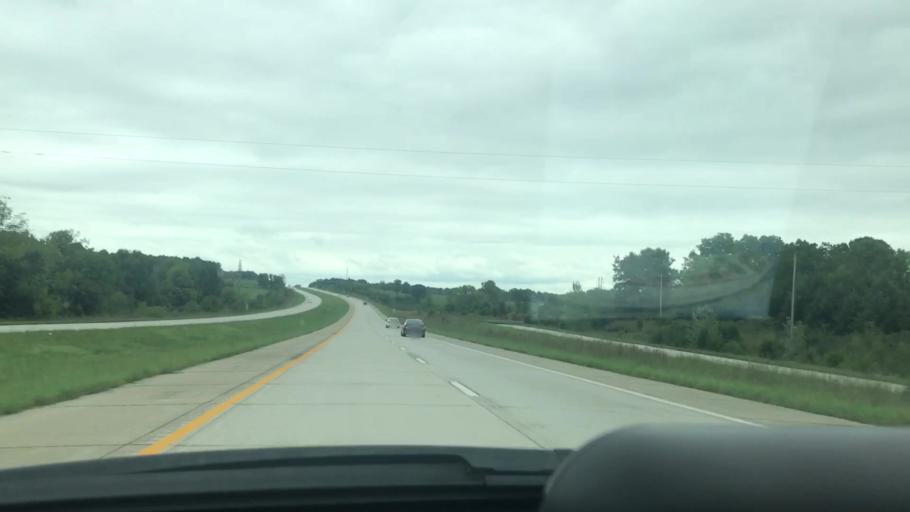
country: US
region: Missouri
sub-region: Dallas County
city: Buffalo
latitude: 37.5272
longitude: -93.1375
